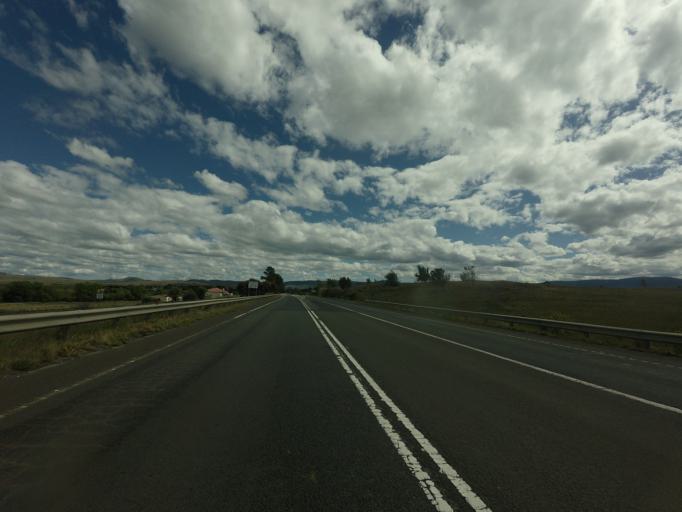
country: AU
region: Tasmania
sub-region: Northern Midlands
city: Evandale
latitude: -42.1288
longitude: 147.4306
